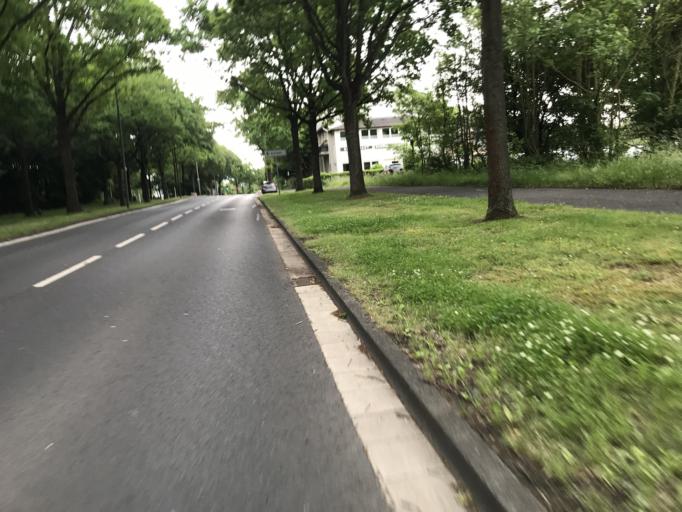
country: DE
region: Hesse
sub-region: Regierungsbezirk Kassel
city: Fuldabruck
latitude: 51.2974
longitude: 9.4390
